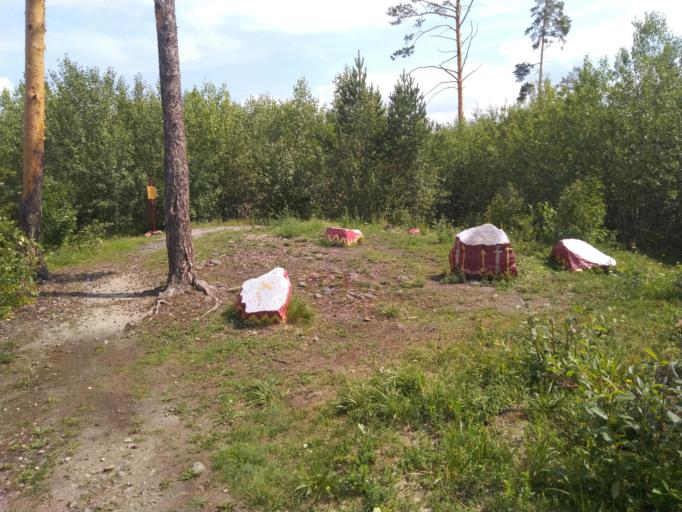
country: RU
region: Sverdlovsk
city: Yekaterinburg
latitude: 56.7685
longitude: 60.6562
